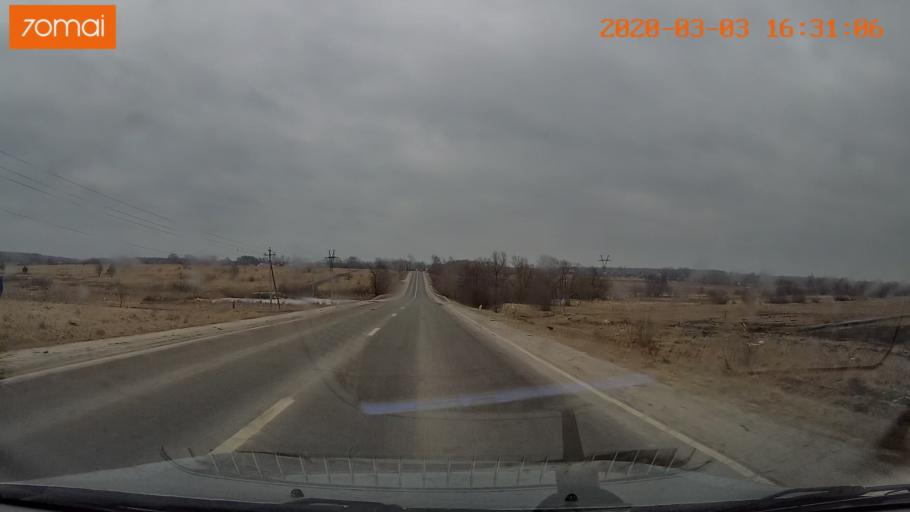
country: RU
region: Moskovskaya
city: Konobeyevo
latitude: 55.4283
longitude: 38.7198
